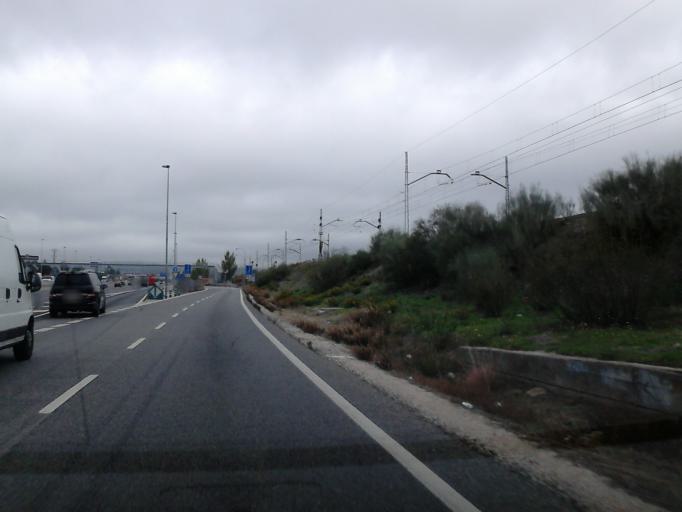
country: ES
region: Madrid
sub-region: Provincia de Madrid
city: Las Matas
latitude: 40.5353
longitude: -3.8886
